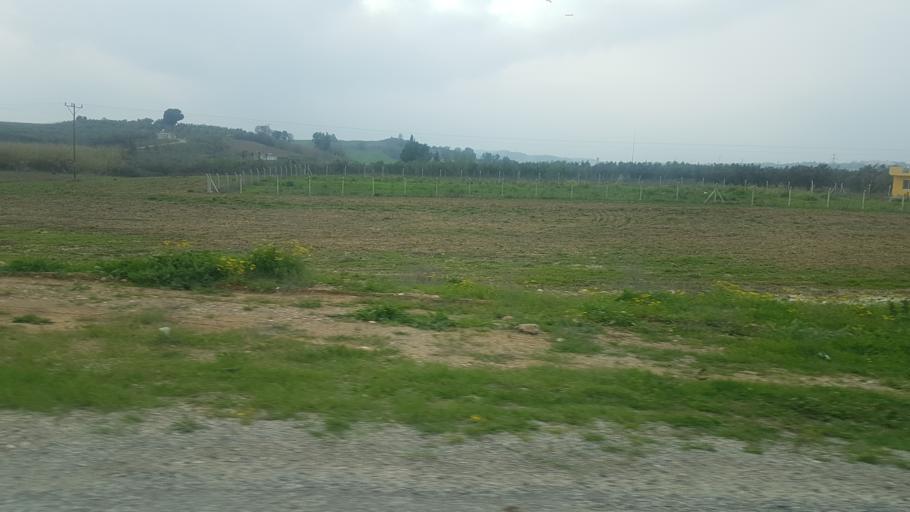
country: TR
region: Mersin
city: Yenice
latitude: 37.0592
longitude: 35.1688
